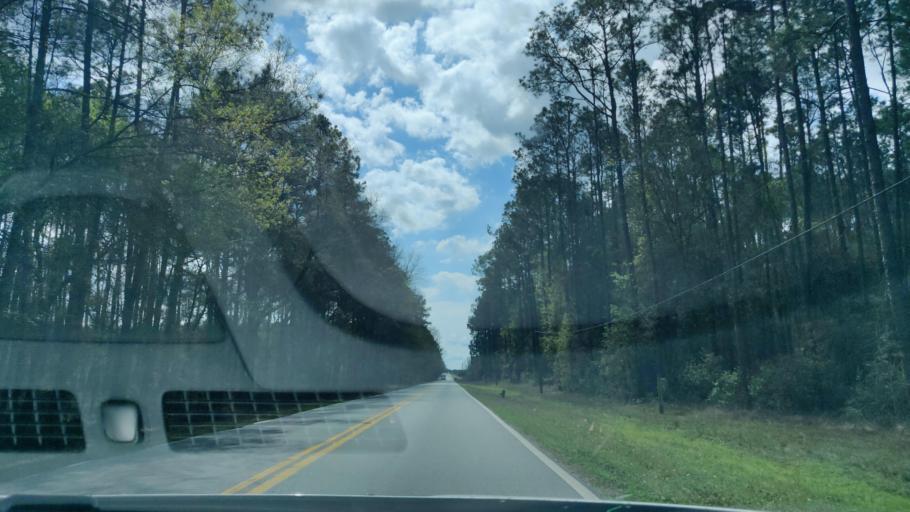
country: US
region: Florida
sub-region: Duval County
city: Baldwin
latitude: 30.2986
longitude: -81.9664
